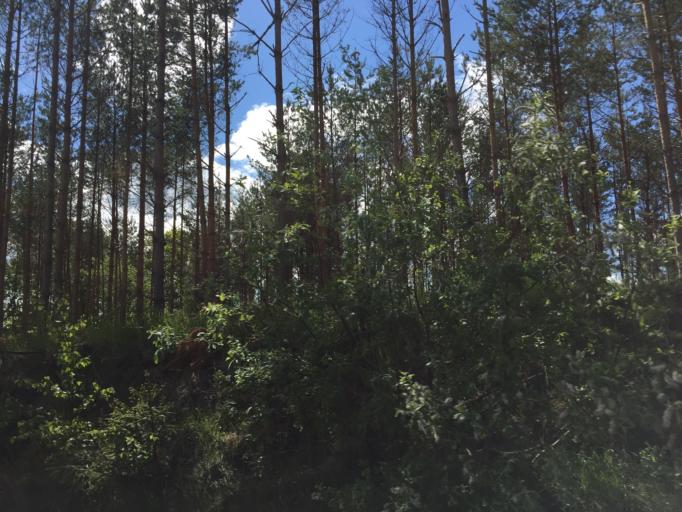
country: SE
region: OEstergoetland
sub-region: Norrkopings Kommun
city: Kimstad
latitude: 58.5281
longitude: 15.9708
